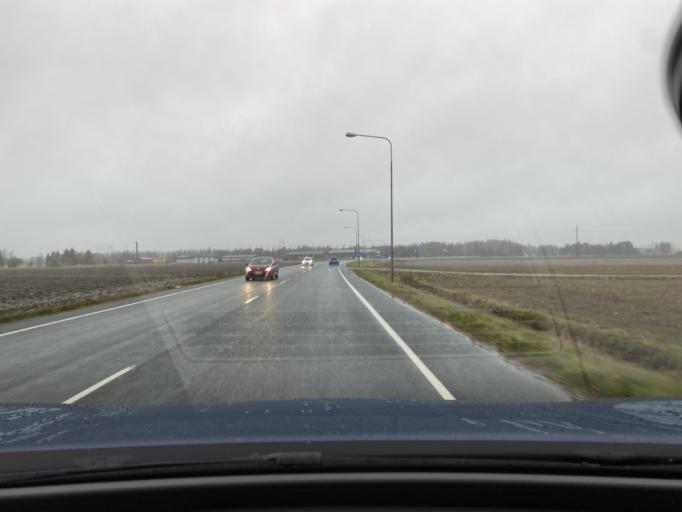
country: FI
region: Varsinais-Suomi
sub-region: Loimaa
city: Loimaa
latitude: 60.8668
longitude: 23.0114
